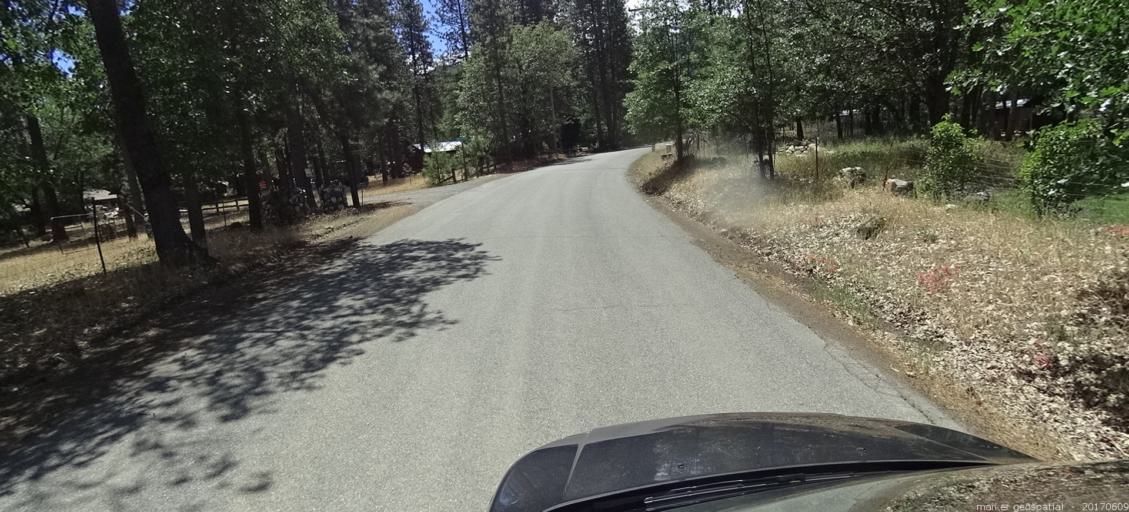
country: US
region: California
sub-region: Siskiyou County
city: Yreka
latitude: 41.4431
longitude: -122.9024
